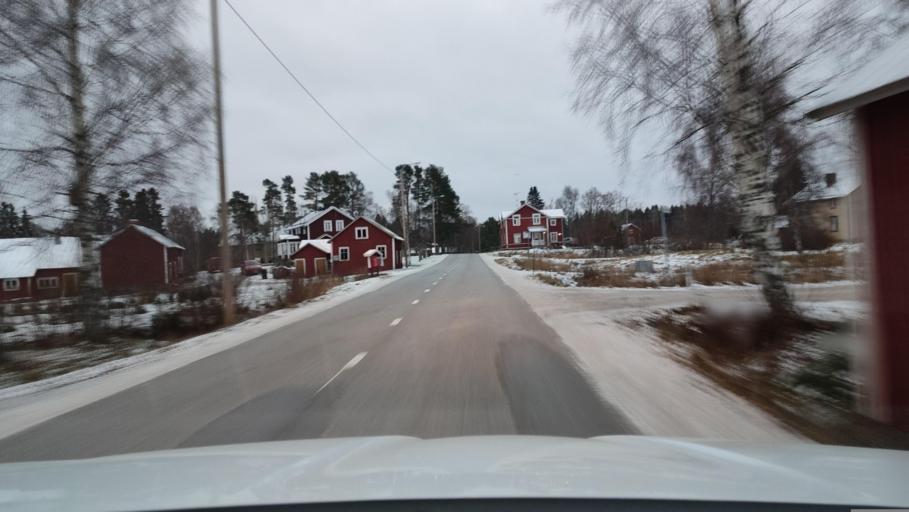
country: FI
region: Ostrobothnia
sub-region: Vaasa
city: Replot
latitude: 63.3403
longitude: 21.3304
